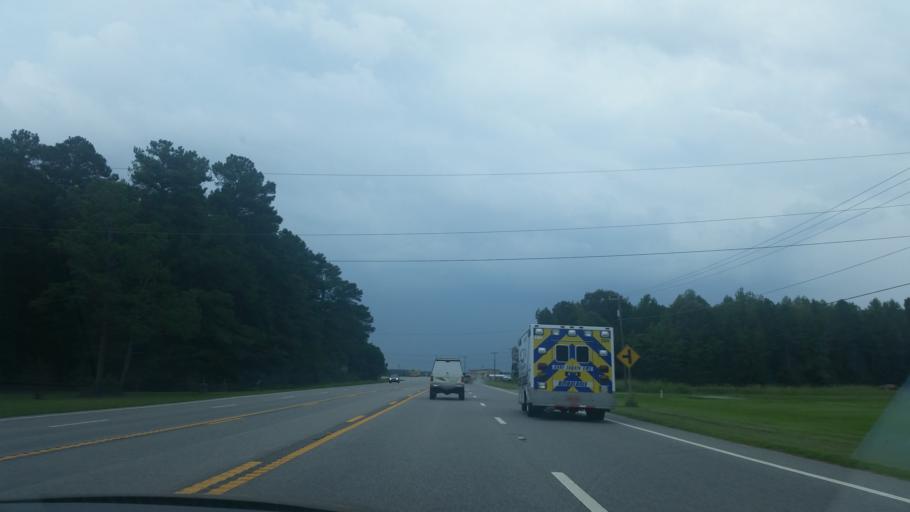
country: US
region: North Carolina
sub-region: Currituck County
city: Currituck
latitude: 36.4635
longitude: -76.1032
